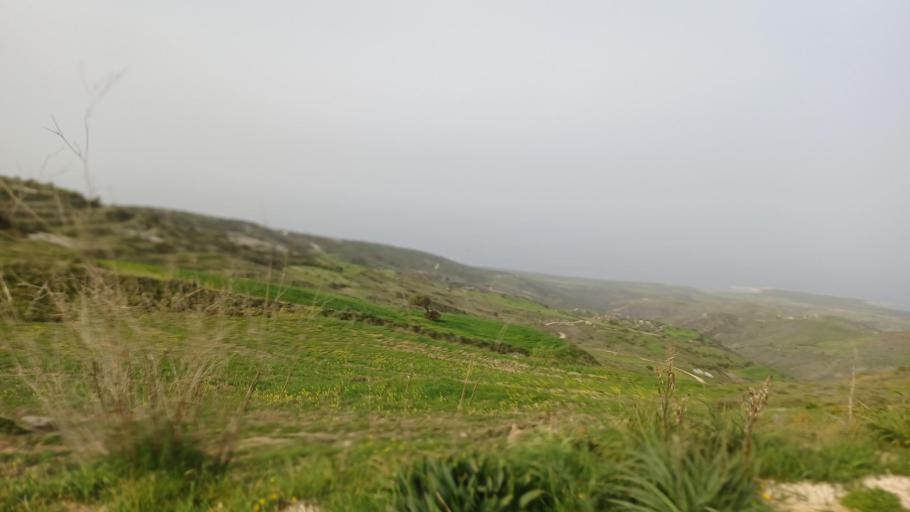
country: CY
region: Pafos
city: Pegeia
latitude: 34.9516
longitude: 32.3791
